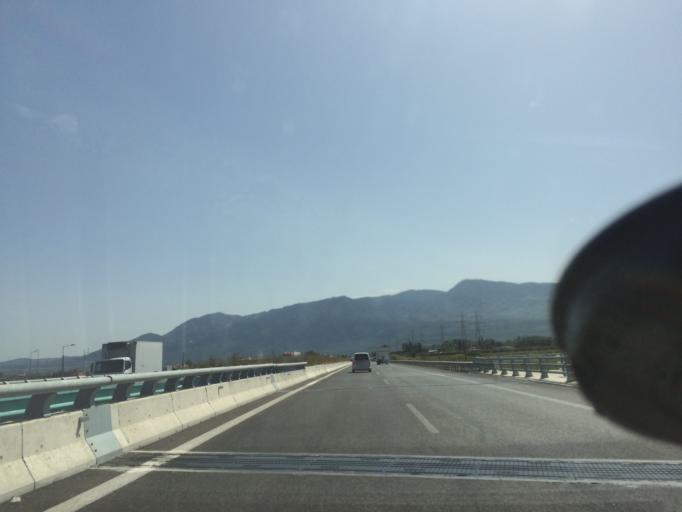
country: GR
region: Central Greece
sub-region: Nomos Fthiotidos
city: Anthili
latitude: 38.8558
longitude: 22.4656
